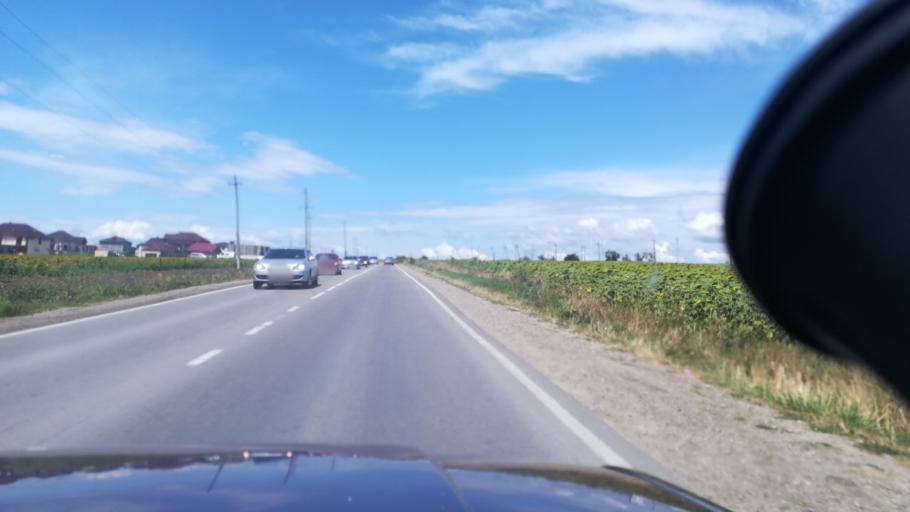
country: RU
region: Krasnodarskiy
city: Tsibanobalka
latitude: 44.9605
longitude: 37.3047
